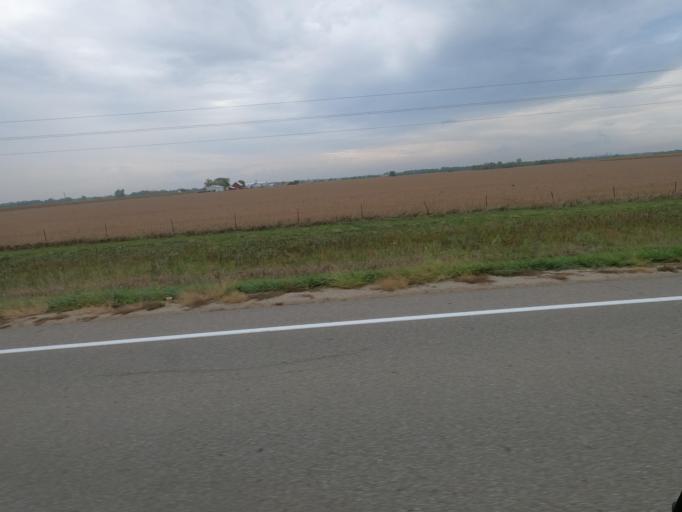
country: US
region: Iowa
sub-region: Henry County
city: Mount Pleasant
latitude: 40.8134
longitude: -91.7358
